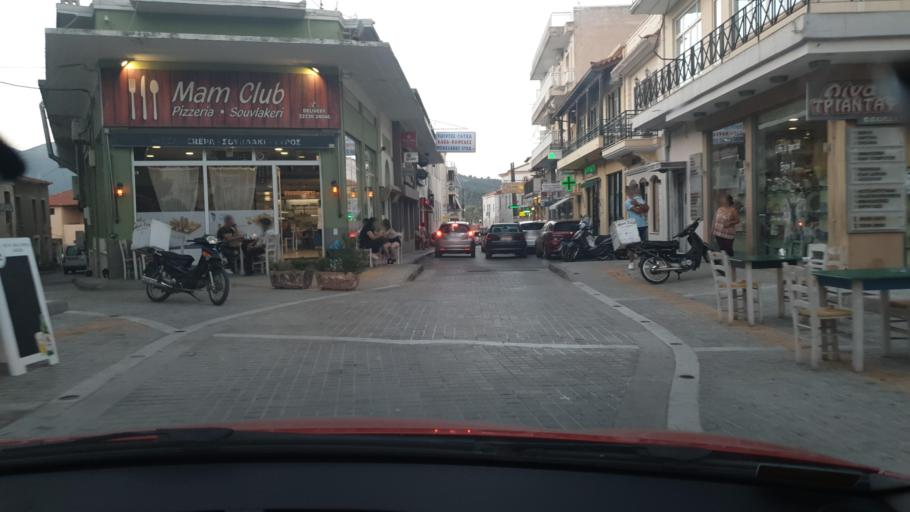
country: GR
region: Central Greece
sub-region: Nomos Evvoias
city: Kymi
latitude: 38.6327
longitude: 24.1037
